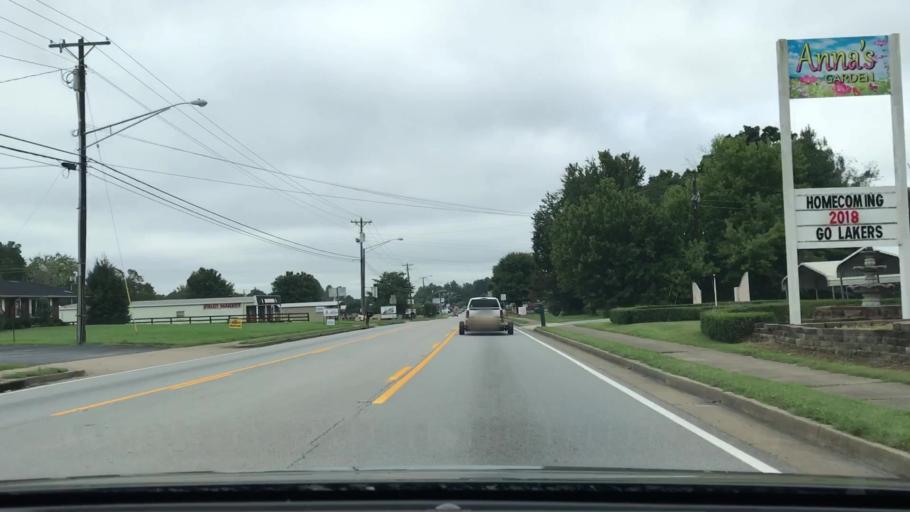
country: US
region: Kentucky
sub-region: Russell County
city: Russell Springs
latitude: 37.0331
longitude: -85.0763
